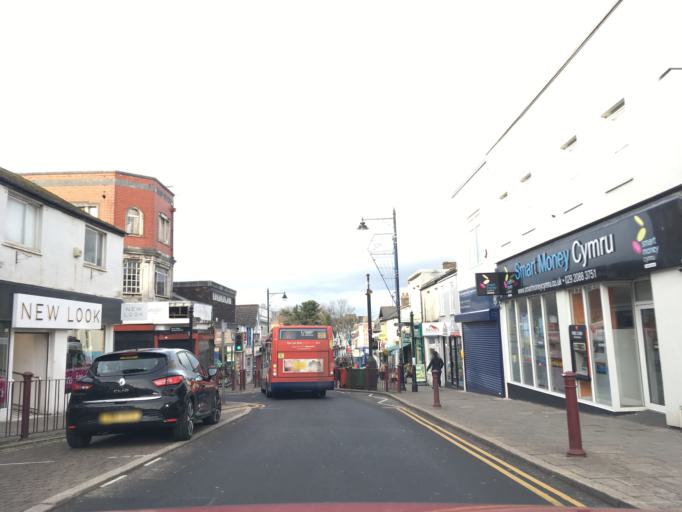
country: GB
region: Wales
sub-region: Caerphilly County Borough
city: Caerphilly
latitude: 51.5727
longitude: -3.2199
